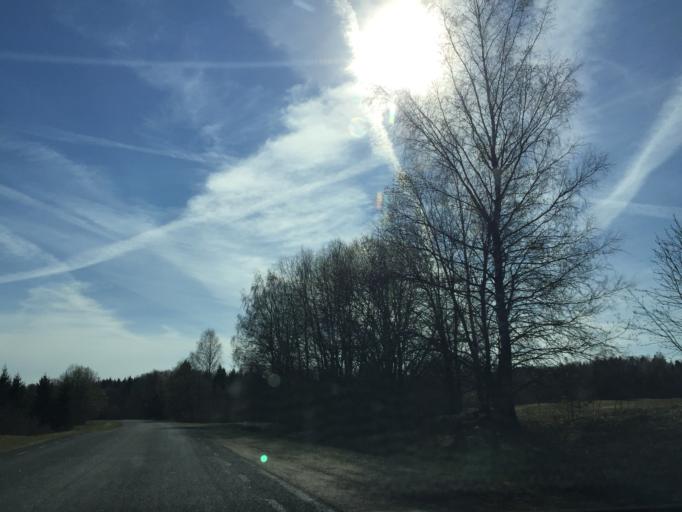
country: EE
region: Vorumaa
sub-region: Antsla vald
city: Vana-Antsla
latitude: 57.9900
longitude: 26.4121
